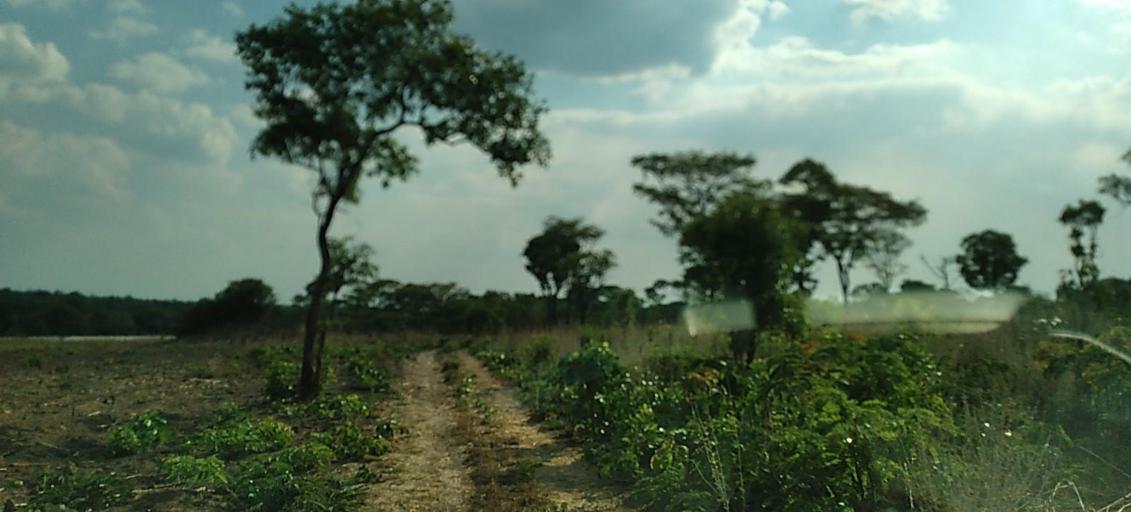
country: ZM
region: Copperbelt
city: Chililabombwe
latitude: -12.3581
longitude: 27.3953
